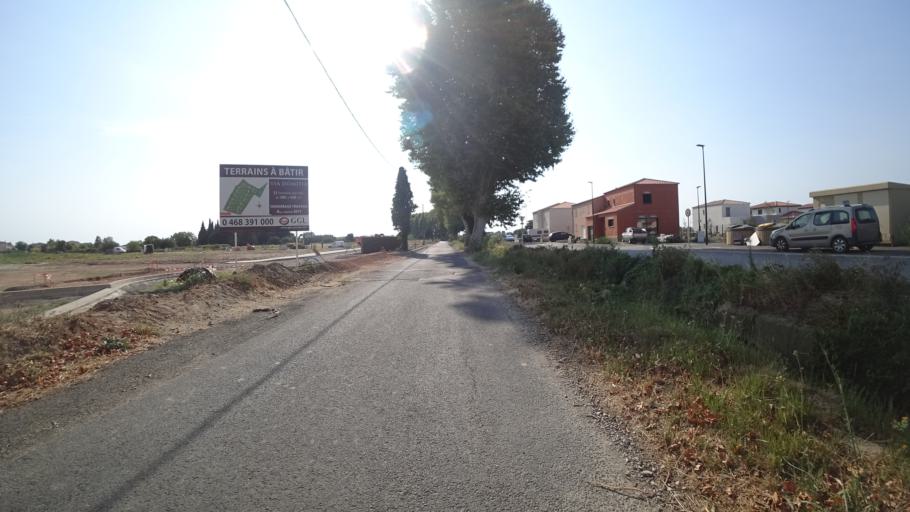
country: FR
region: Languedoc-Roussillon
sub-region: Departement des Pyrenees-Orientales
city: Claira
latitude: 42.7599
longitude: 2.9609
